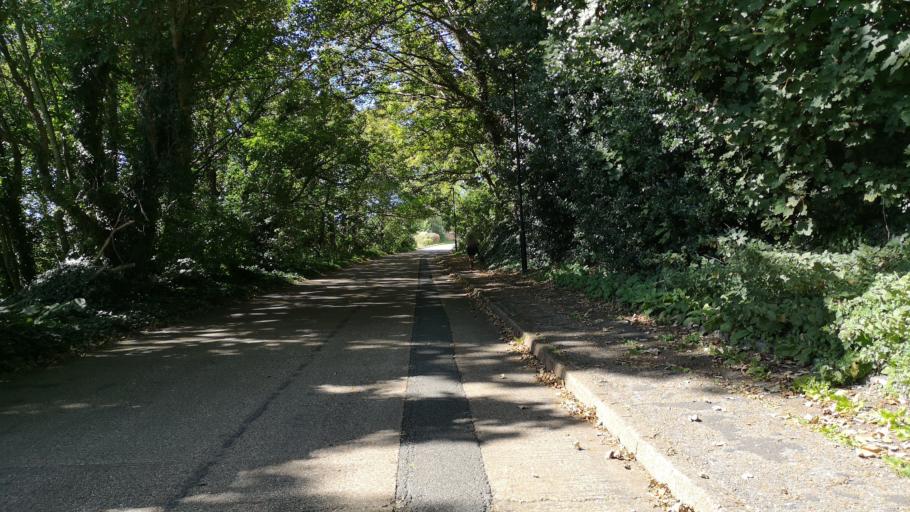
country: GB
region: England
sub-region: Isle of Wight
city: Ventnor
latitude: 50.5918
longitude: -1.2239
